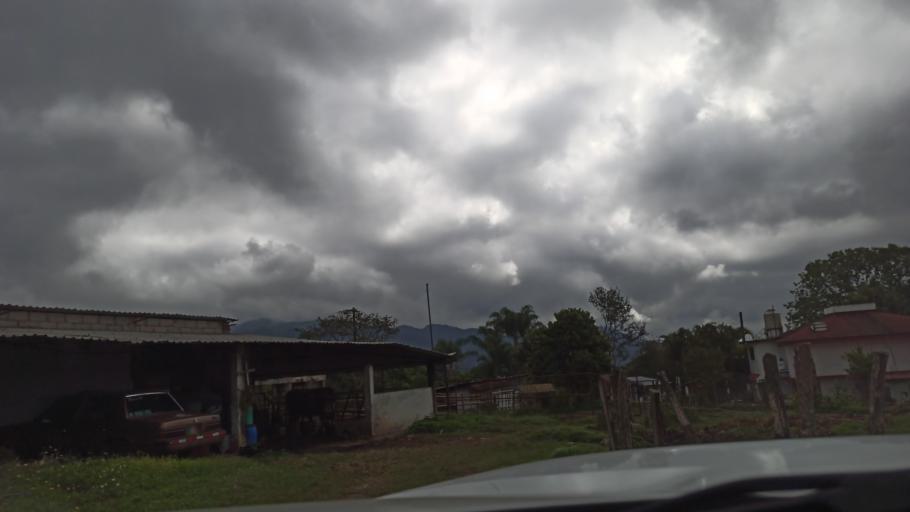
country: MX
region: Veracruz
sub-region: Chocaman
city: San Jose Neria
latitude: 19.0001
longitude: -97.0016
